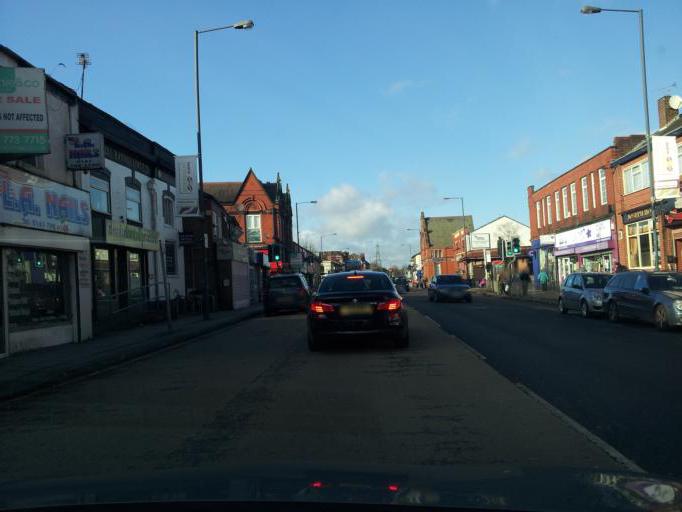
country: GB
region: England
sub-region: Borough of Bury
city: Prestwich
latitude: 53.5319
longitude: -2.2844
